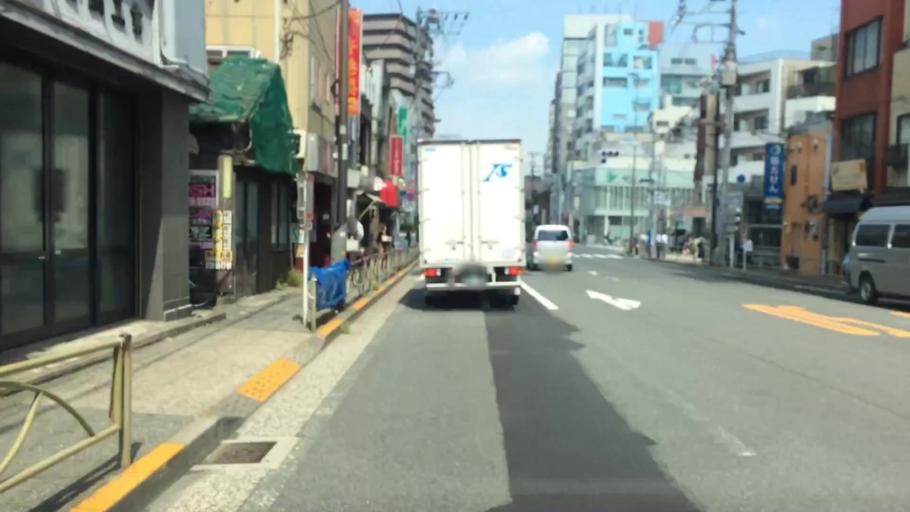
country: JP
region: Tokyo
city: Tokyo
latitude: 35.7249
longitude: 139.7304
